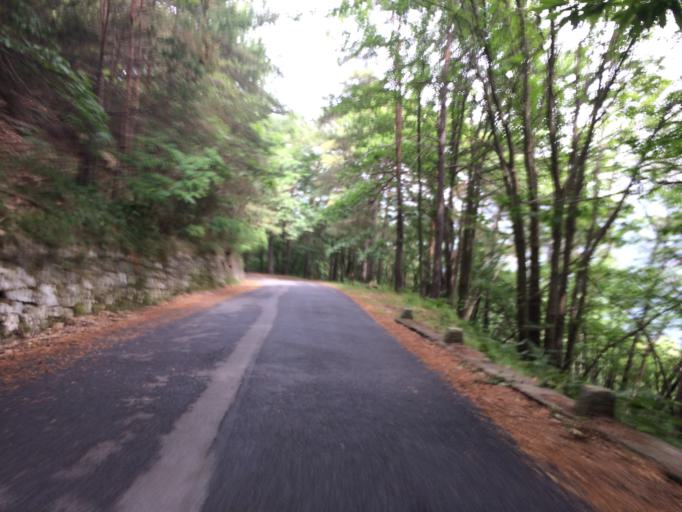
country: IT
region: Liguria
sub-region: Provincia di Imperia
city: Bajardo
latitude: 43.8934
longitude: 7.7328
